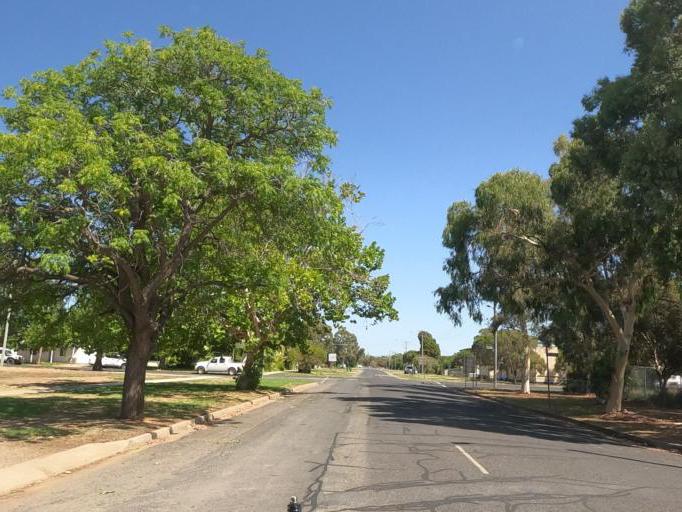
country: AU
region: New South Wales
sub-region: Corowa Shire
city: Mulwala
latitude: -35.9875
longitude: 146.0061
